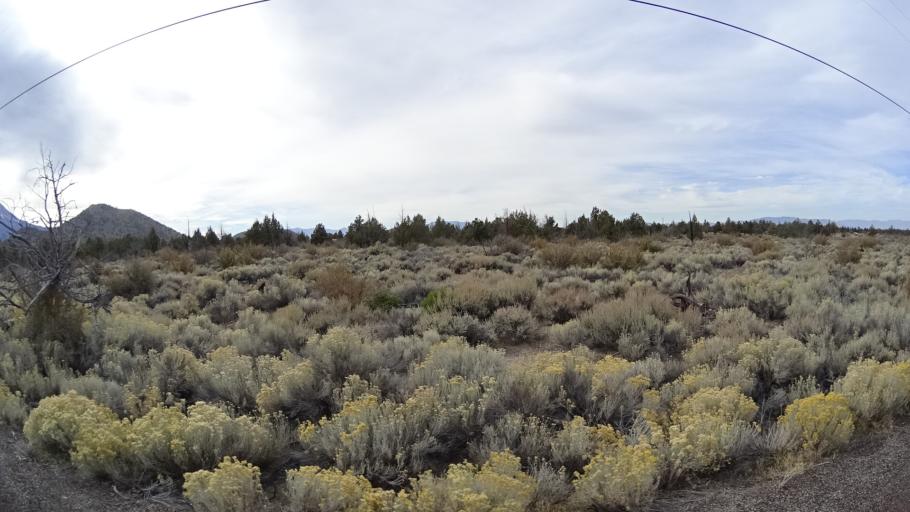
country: US
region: California
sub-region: Siskiyou County
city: Weed
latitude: 41.5611
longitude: -122.2602
